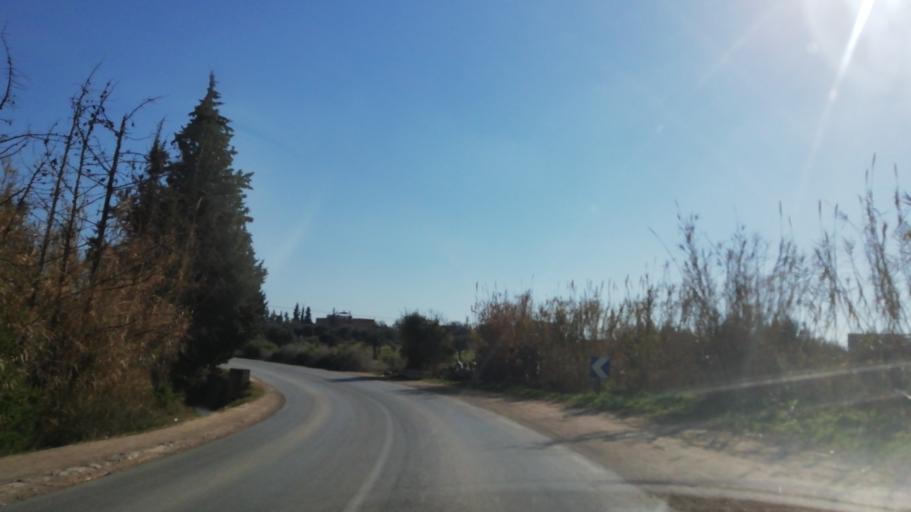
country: DZ
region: Tlemcen
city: Nedroma
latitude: 34.8321
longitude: -1.6952
